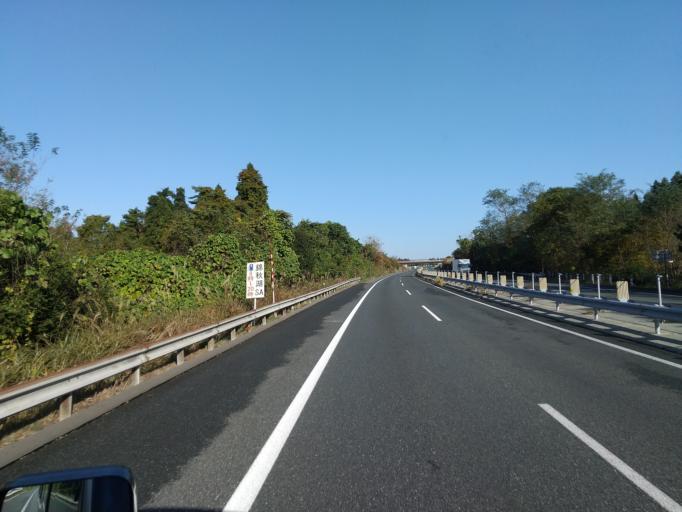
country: JP
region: Iwate
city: Mizusawa
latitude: 39.0535
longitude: 141.1066
